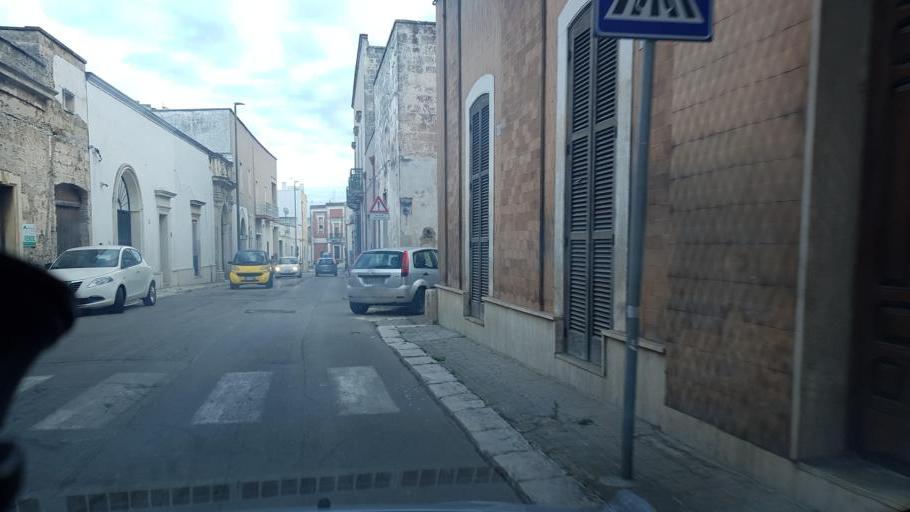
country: IT
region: Apulia
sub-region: Provincia di Lecce
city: Veglie
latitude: 40.3363
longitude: 17.9709
